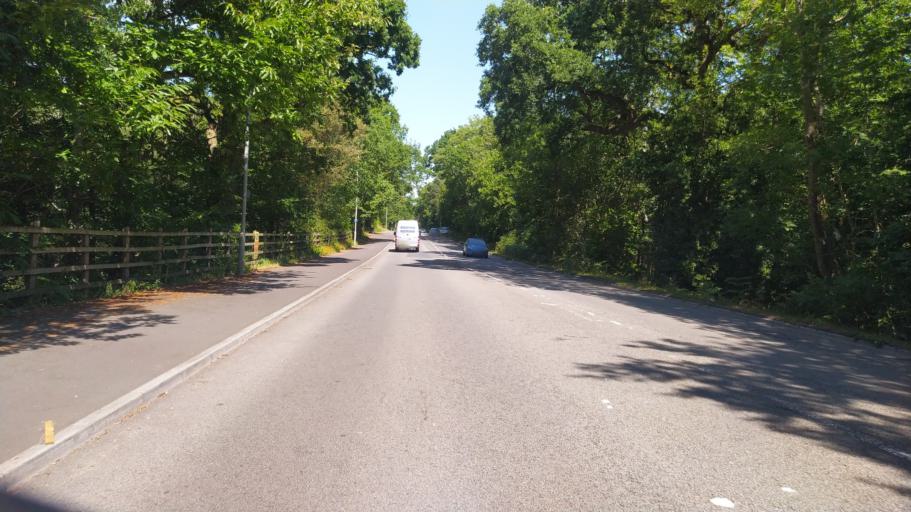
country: GB
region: England
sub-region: Dorset
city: Wimborne Minster
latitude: 50.7671
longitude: -1.9788
